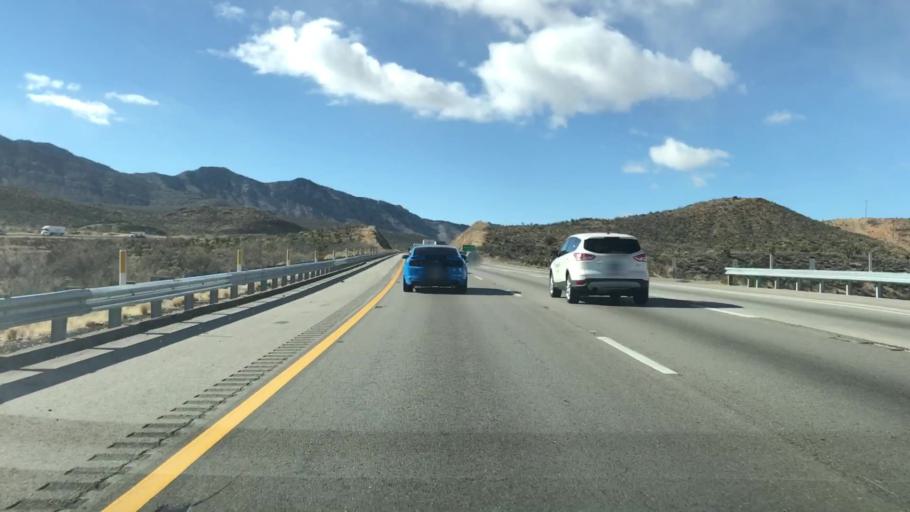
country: US
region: Nevada
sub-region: Clark County
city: Sandy Valley
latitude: 35.4710
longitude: -115.5075
